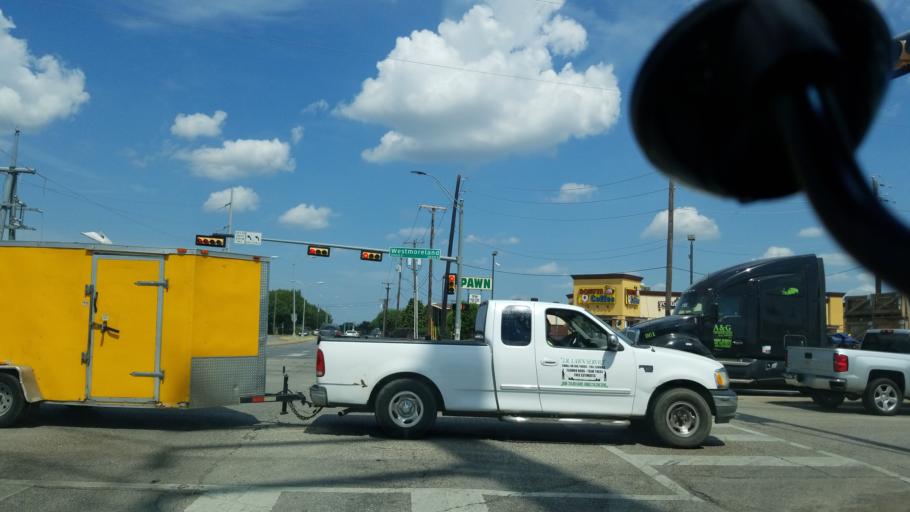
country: US
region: Texas
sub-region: Dallas County
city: Cockrell Hill
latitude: 32.7203
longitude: -96.8745
